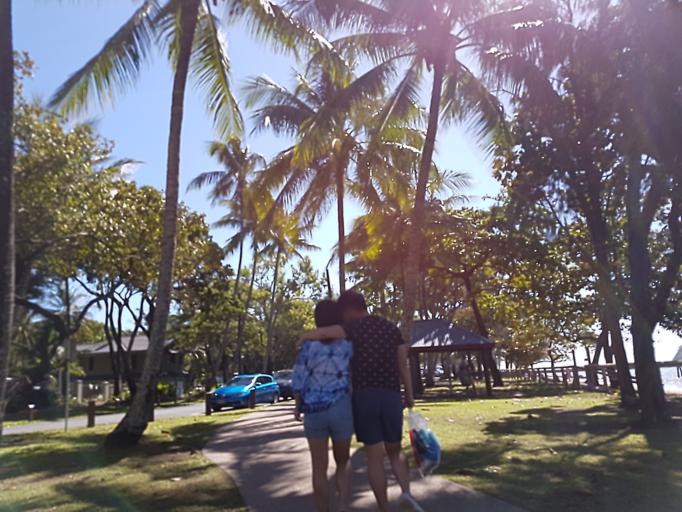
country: AU
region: Queensland
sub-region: Cairns
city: Palm Cove
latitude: -16.7413
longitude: 145.6714
